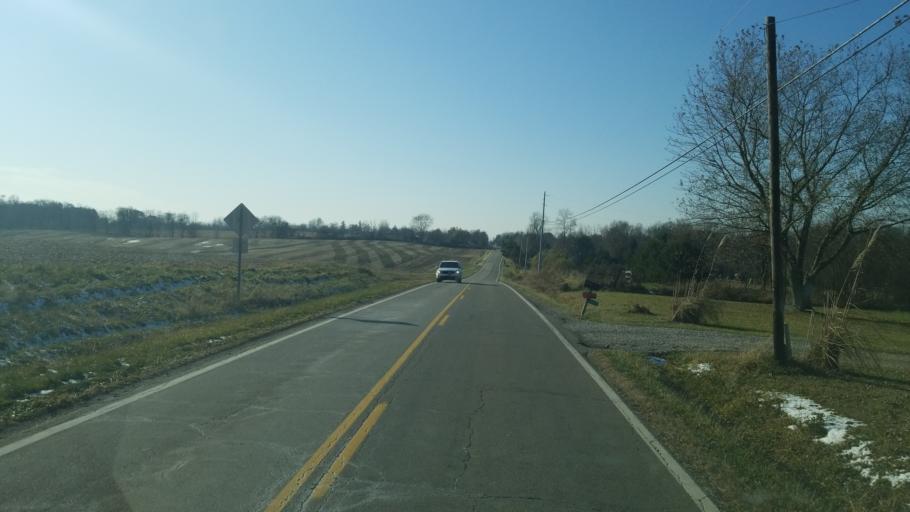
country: US
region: Ohio
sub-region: Licking County
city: Granville
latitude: 40.1513
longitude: -82.5076
